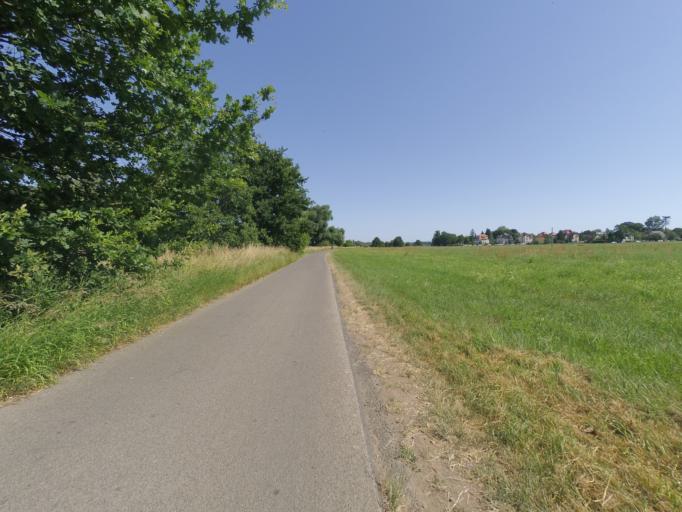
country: DE
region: Saxony
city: Heidenau
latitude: 51.0333
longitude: 13.8350
